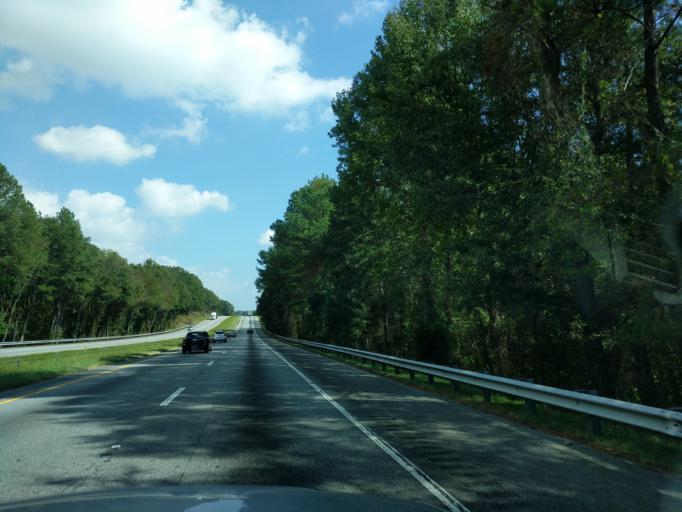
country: US
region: South Carolina
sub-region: Anderson County
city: Centerville
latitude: 34.5629
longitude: -82.7571
